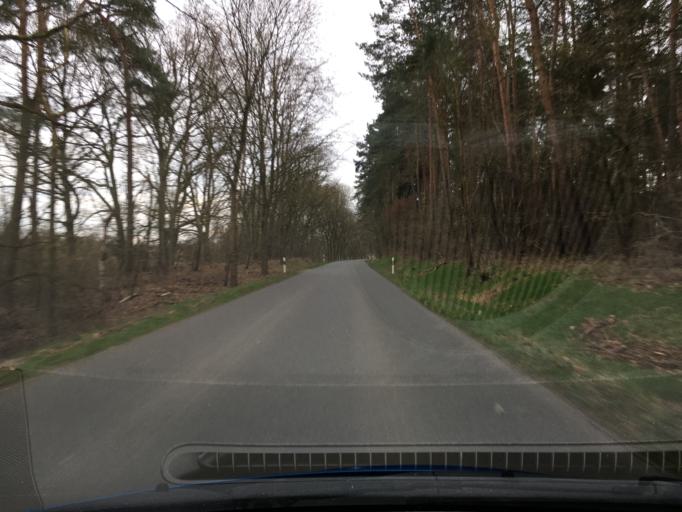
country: DE
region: Lower Saxony
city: Bad Bevensen
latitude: 53.0513
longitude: 10.6020
